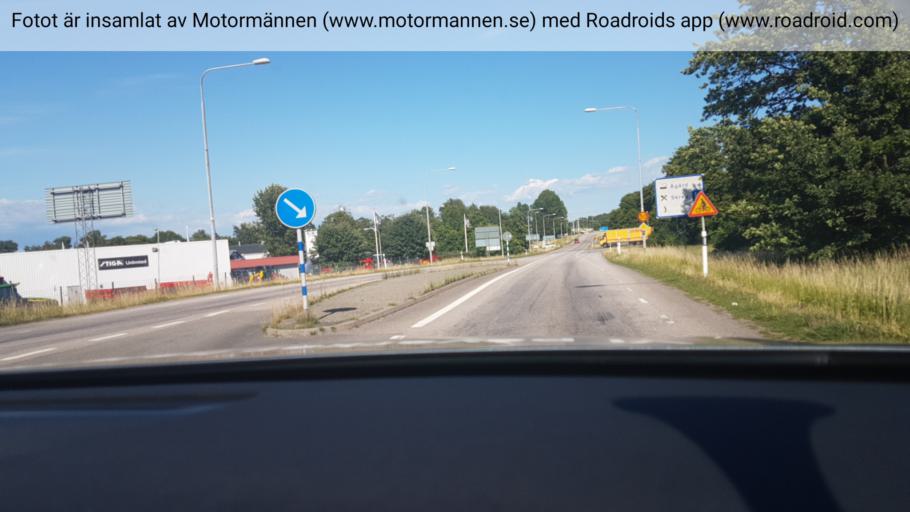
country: SE
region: Halland
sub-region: Falkenbergs Kommun
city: Falkenberg
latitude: 56.8989
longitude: 12.5310
